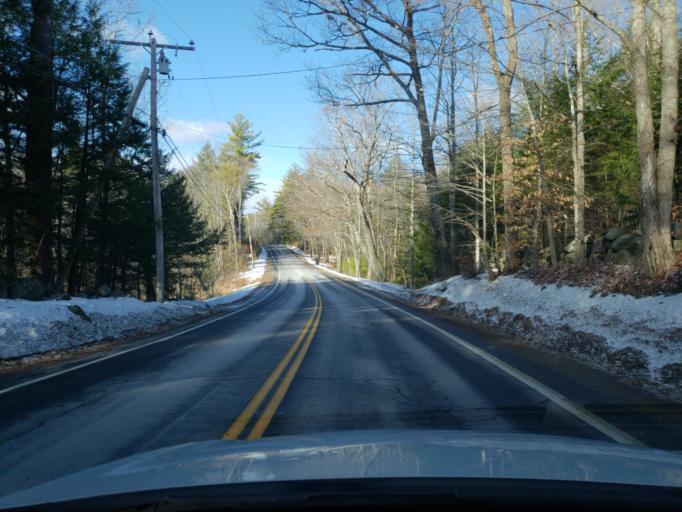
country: US
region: New Hampshire
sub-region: Hillsborough County
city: New Boston
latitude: 42.9839
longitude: -71.6951
